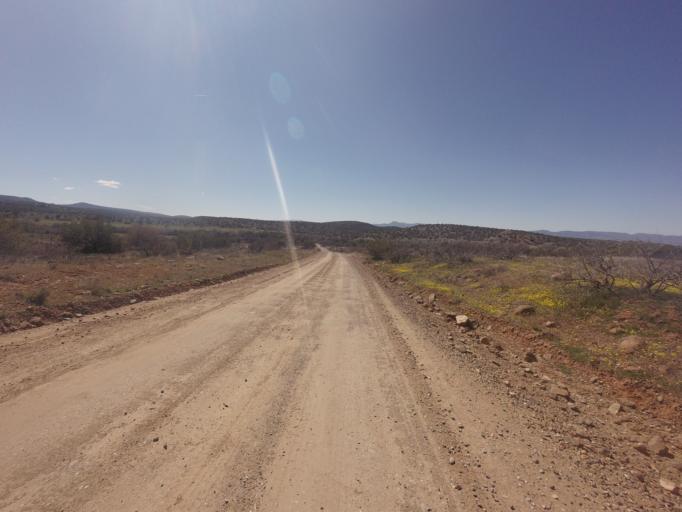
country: US
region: Arizona
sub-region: Yavapai County
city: Lake Montezuma
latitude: 34.6517
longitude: -111.7190
